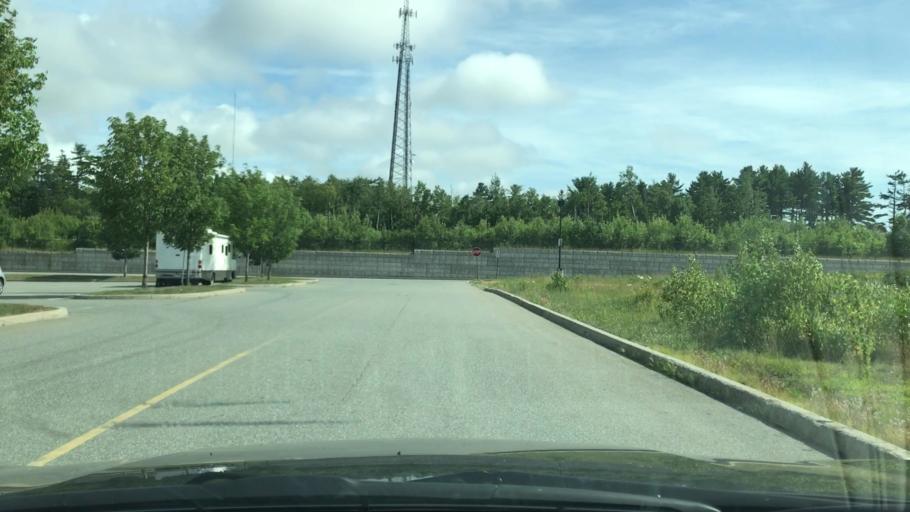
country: US
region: Maine
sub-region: Hancock County
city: Ellsworth
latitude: 44.5241
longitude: -68.3953
